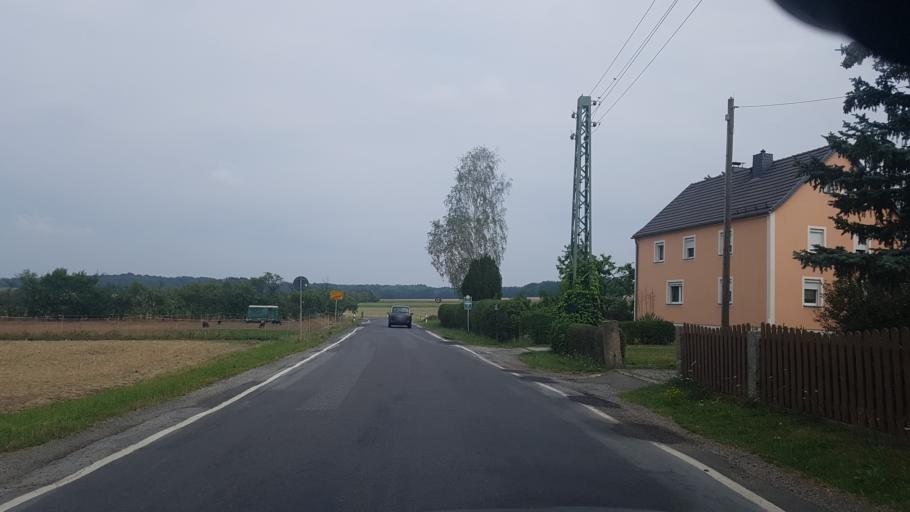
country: DE
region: Saxony
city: Crostwitz
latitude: 51.2399
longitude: 14.2470
